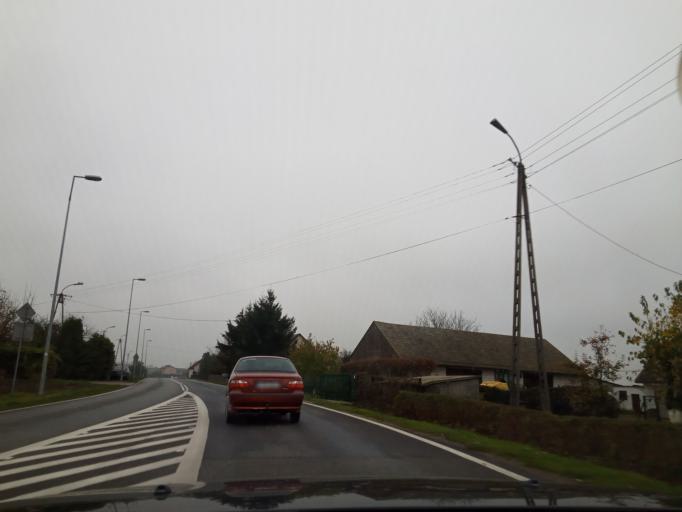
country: PL
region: Lesser Poland Voivodeship
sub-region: Powiat proszowicki
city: Klimontow
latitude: 50.2287
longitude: 20.3700
